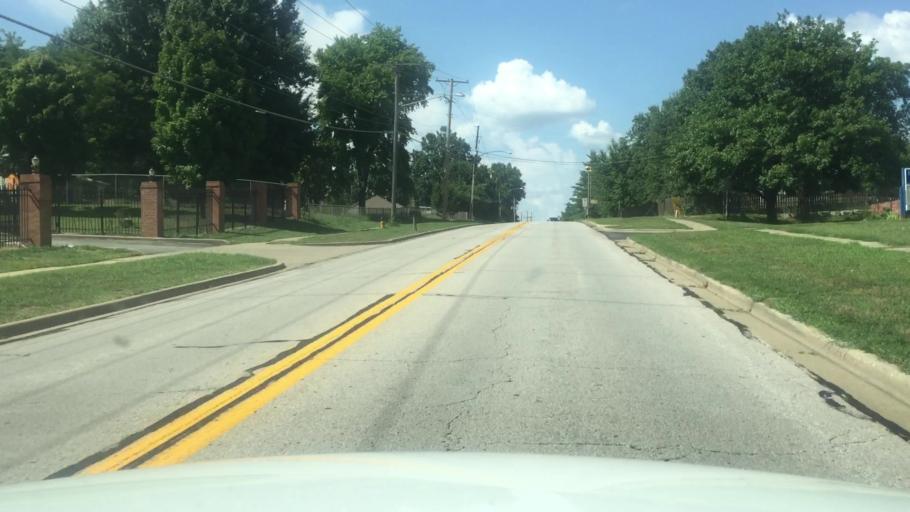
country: US
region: Kansas
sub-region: Johnson County
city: Shawnee
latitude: 39.0036
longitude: -94.7424
